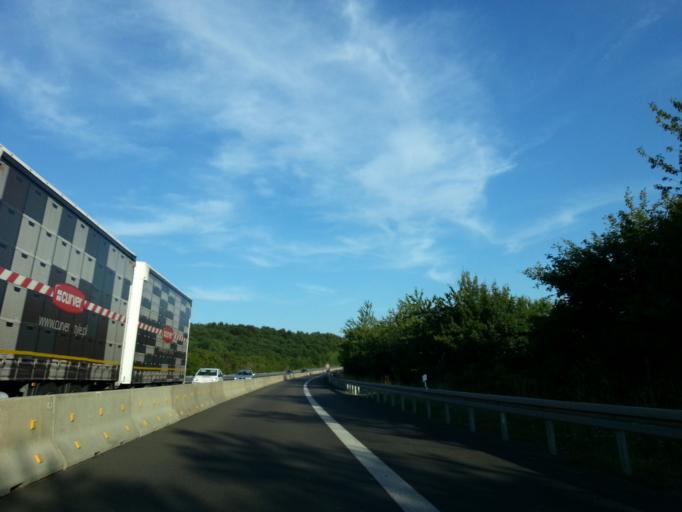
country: DE
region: Rheinland-Pfalz
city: Neuhutten
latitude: 49.5961
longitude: 6.9981
